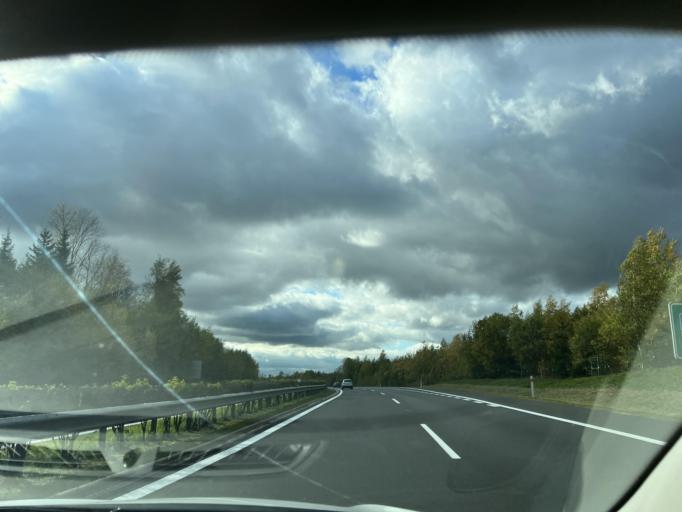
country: CZ
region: Karlovarsky
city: Brezova
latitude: 50.1509
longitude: 12.6461
